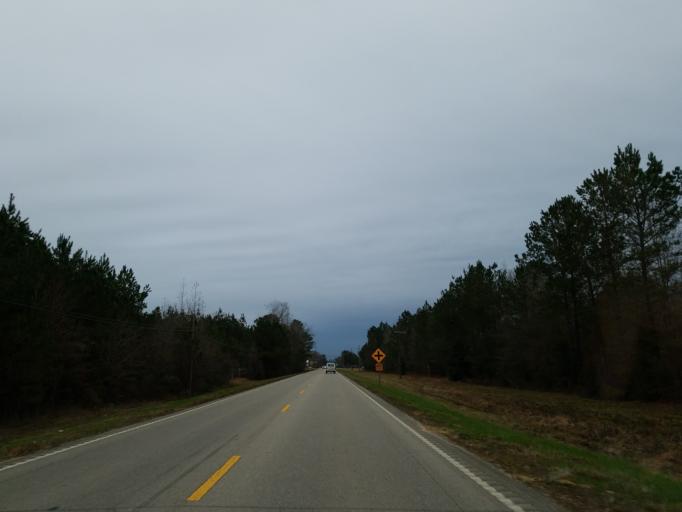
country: US
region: Mississippi
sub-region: Forrest County
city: Glendale
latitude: 31.4304
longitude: -89.2828
